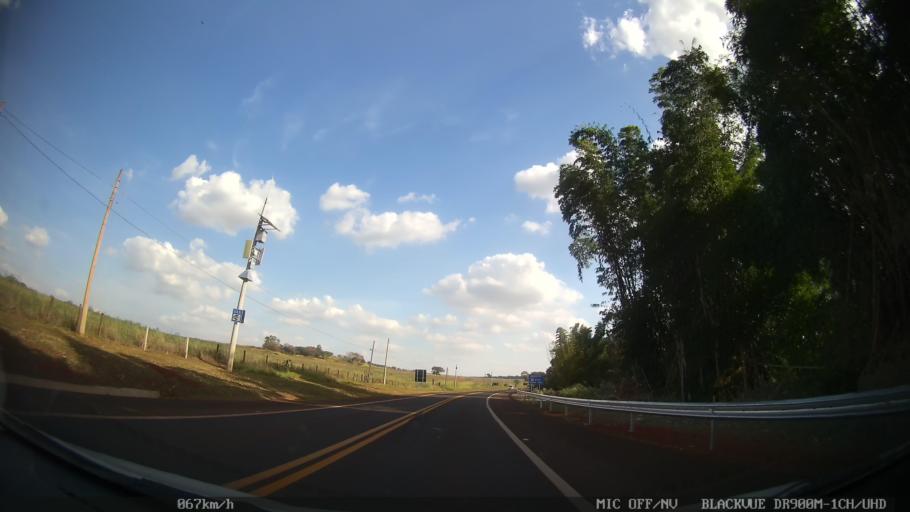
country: BR
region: Sao Paulo
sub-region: Ribeirao Preto
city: Ribeirao Preto
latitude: -21.1905
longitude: -47.8661
